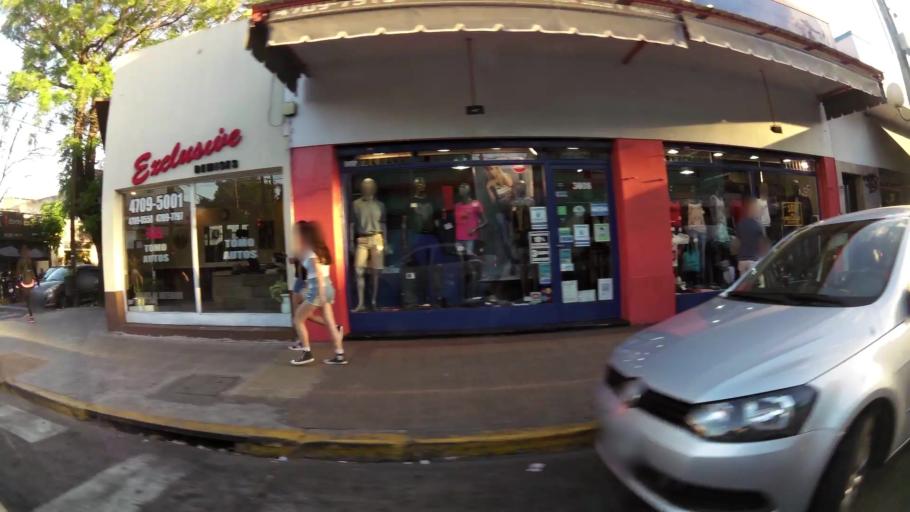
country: AR
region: Buenos Aires
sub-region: Partido de General San Martin
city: General San Martin
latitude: -34.5482
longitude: -58.5046
